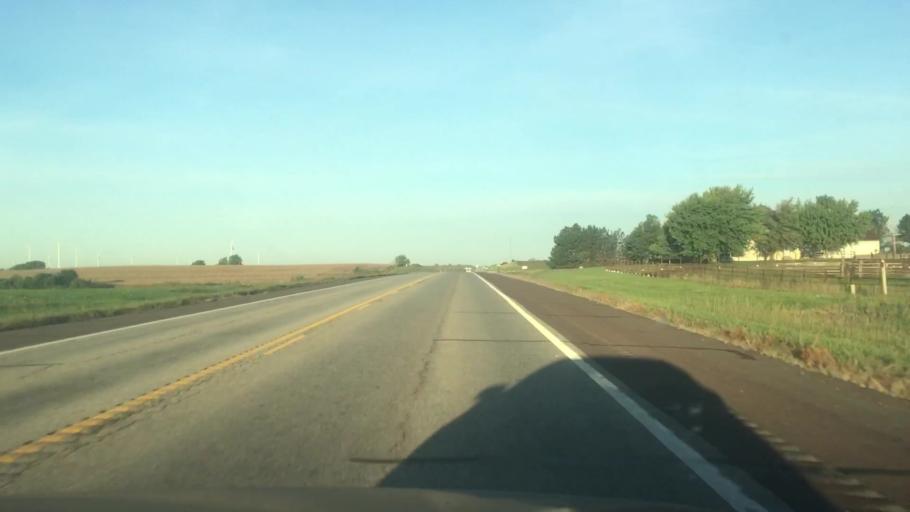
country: US
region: Kansas
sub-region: Nemaha County
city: Seneca
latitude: 39.8422
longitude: -96.3173
